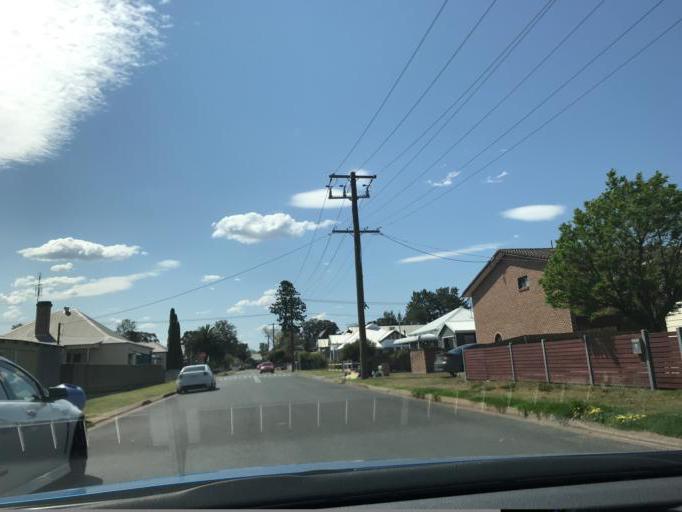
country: AU
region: New South Wales
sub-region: Singleton
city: Singleton
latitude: -32.5662
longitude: 151.1725
